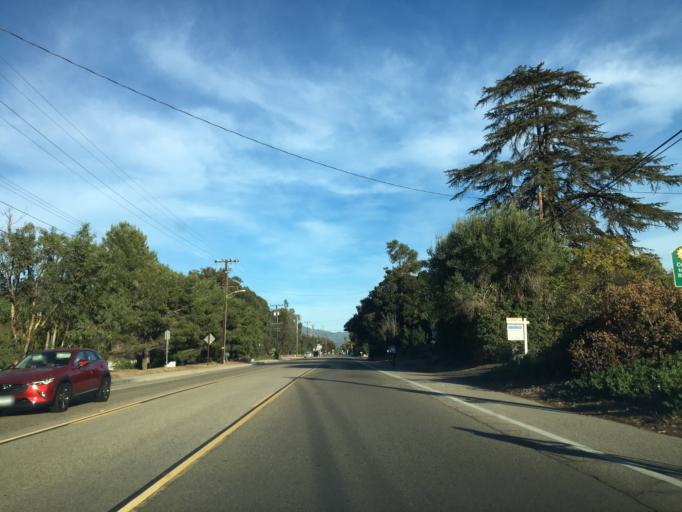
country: US
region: California
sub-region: Santa Barbara County
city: Goleta
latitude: 34.4385
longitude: -119.7790
